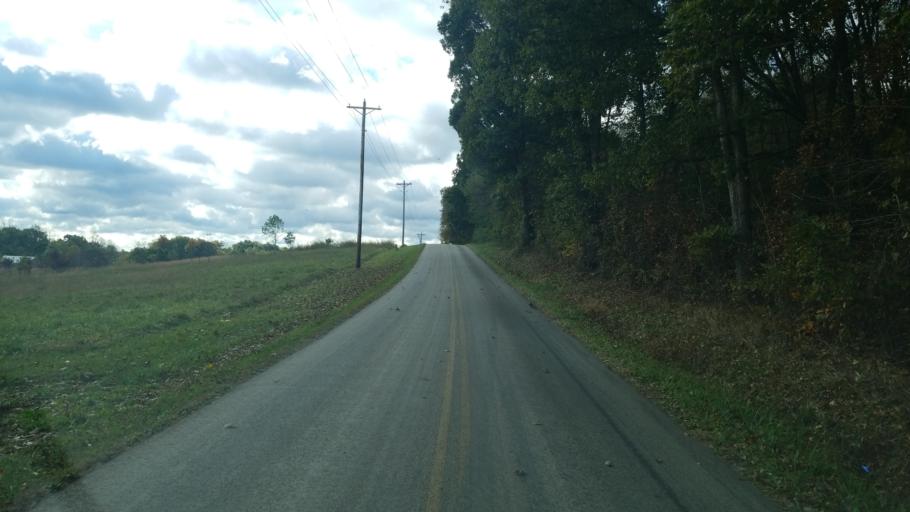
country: US
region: Ohio
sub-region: Vinton County
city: McArthur
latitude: 39.2316
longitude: -82.5086
